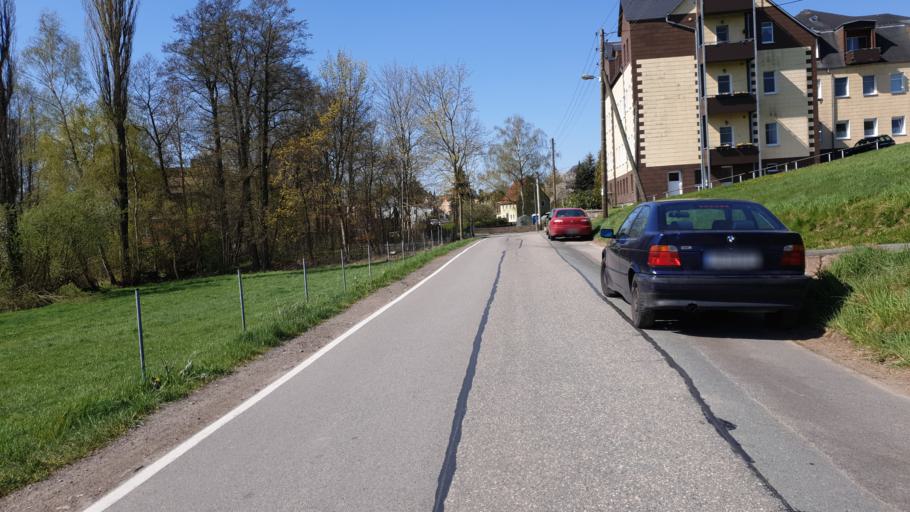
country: DE
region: Saxony
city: Claussnitz
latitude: 50.9099
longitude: 12.8774
